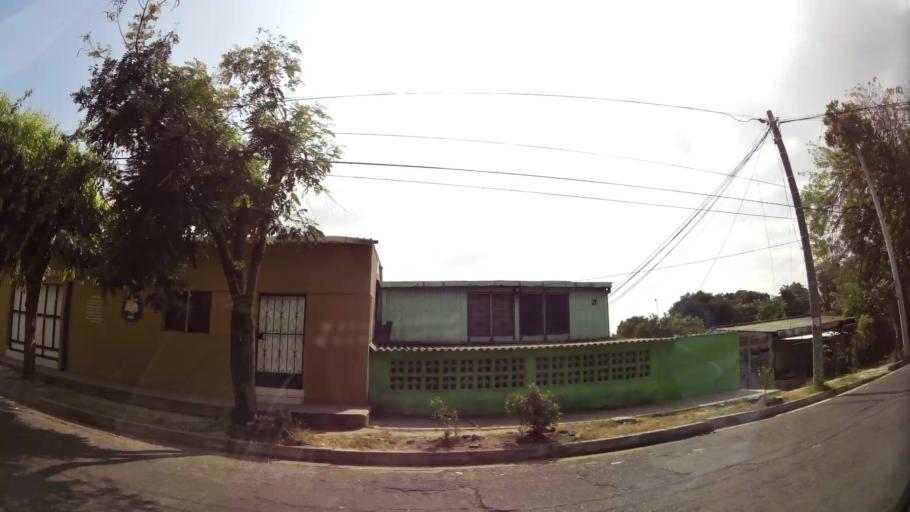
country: SV
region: San Salvador
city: Delgado
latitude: 13.7110
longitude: -89.1693
